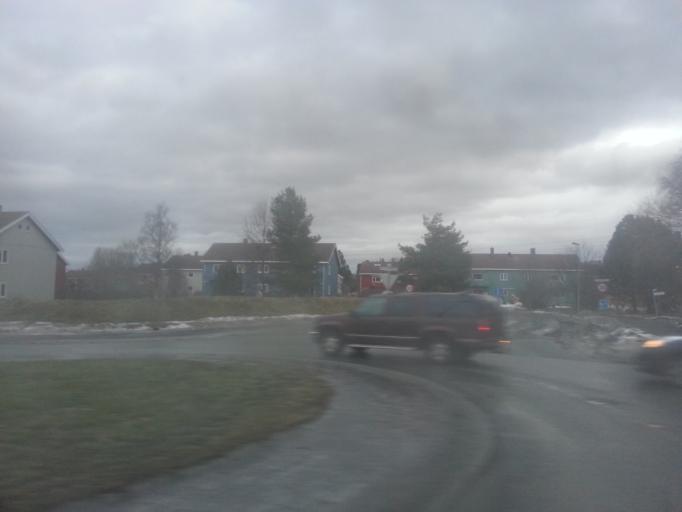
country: NO
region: Sor-Trondelag
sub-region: Trondheim
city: Trondheim
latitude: 63.4301
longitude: 10.4545
